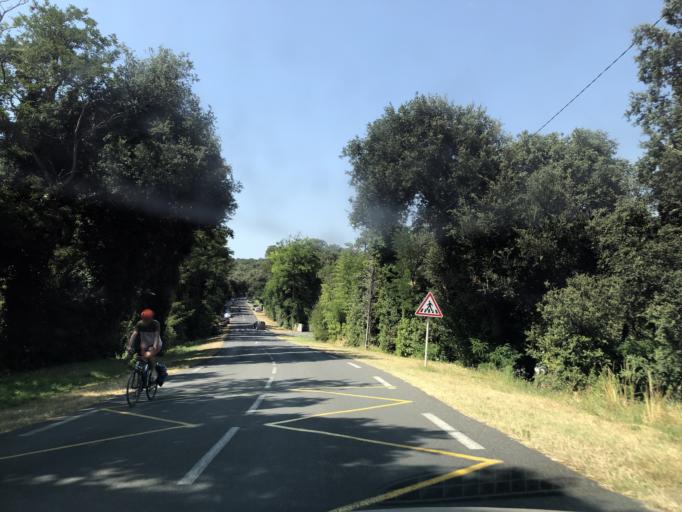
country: FR
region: Poitou-Charentes
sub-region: Departement de la Charente-Maritime
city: Meschers-sur-Gironde
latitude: 45.5648
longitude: -0.9695
